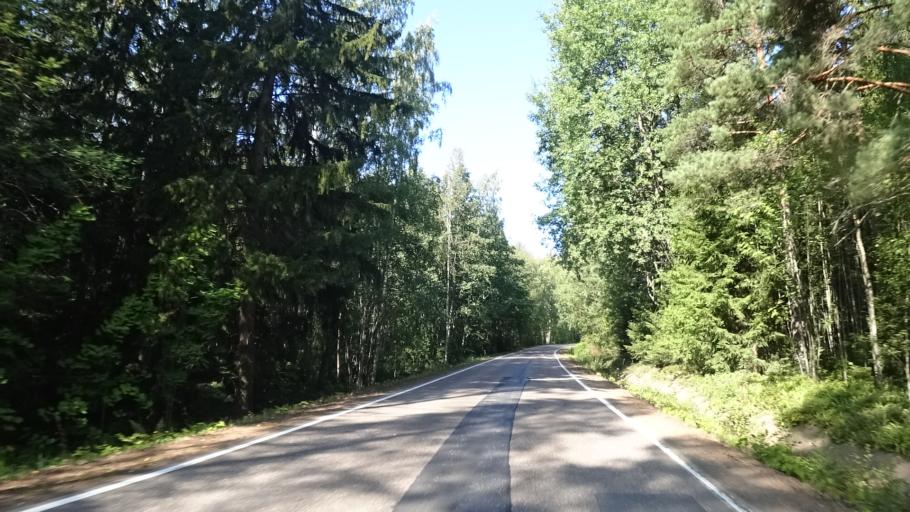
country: FI
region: Kymenlaakso
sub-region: Kotka-Hamina
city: Hamina
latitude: 60.5384
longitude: 27.2723
